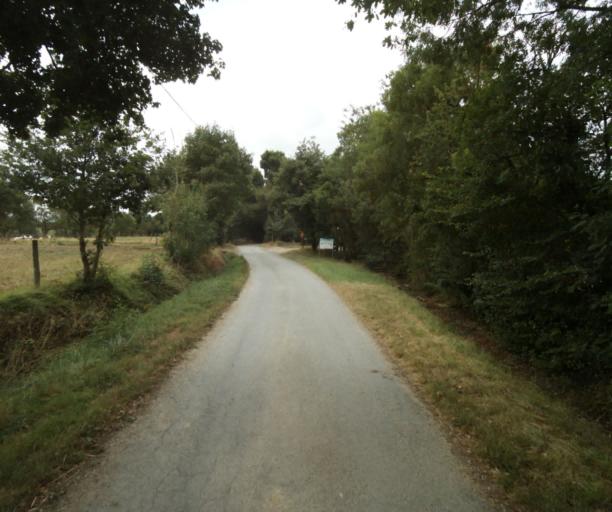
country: FR
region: Midi-Pyrenees
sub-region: Departement du Tarn
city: Soreze
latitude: 43.4776
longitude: 2.0445
